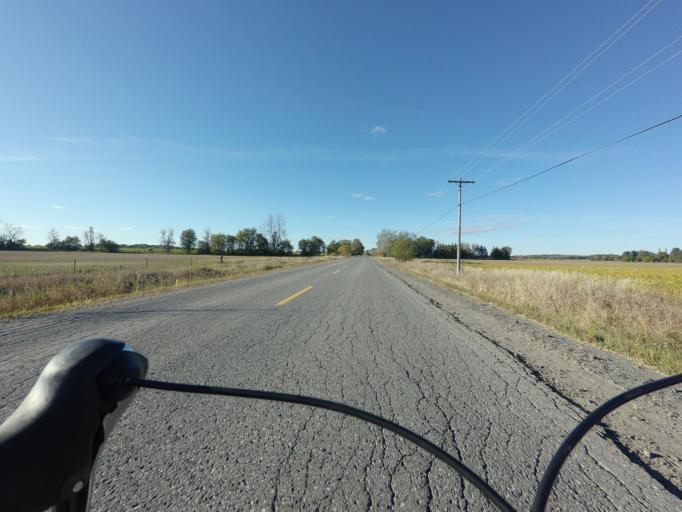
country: CA
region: Ontario
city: Bells Corners
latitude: 45.2095
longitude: -75.7956
